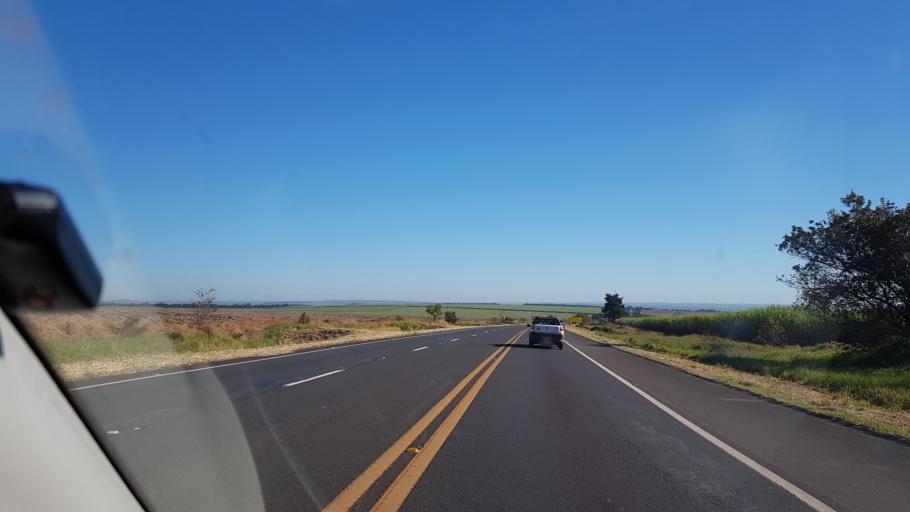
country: BR
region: Sao Paulo
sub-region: Assis
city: Assis
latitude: -22.5683
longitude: -50.5212
